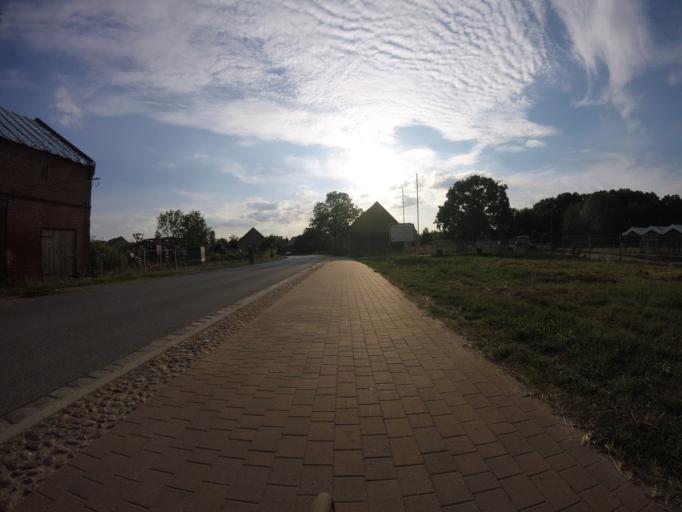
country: DE
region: Brandenburg
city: Altlandsberg
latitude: 52.5653
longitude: 13.7344
